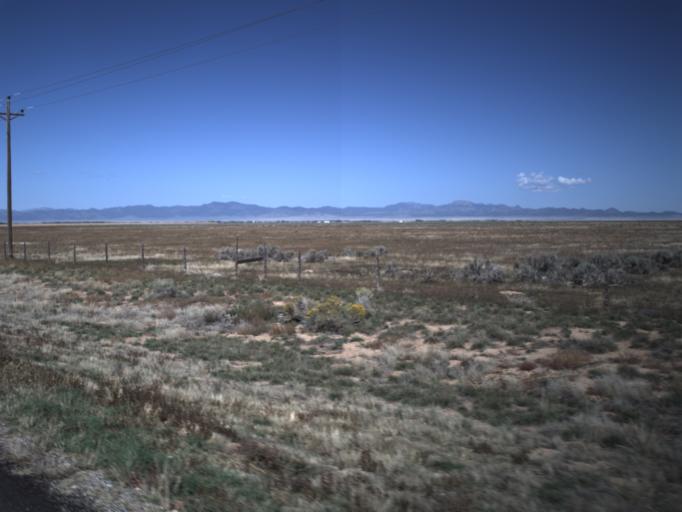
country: US
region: Utah
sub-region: Washington County
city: Enterprise
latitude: 37.6808
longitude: -113.5764
